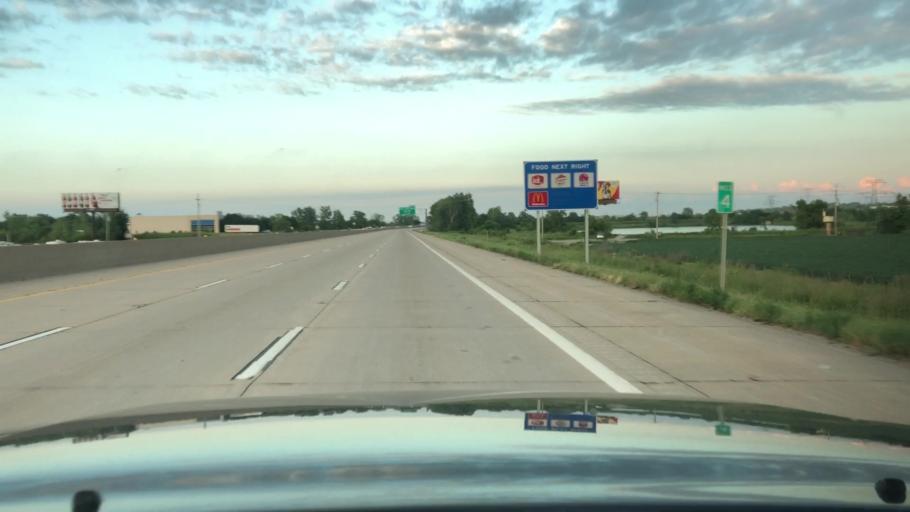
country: US
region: Missouri
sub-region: Saint Charles County
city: Saint Charles
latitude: 38.8242
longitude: -90.5330
